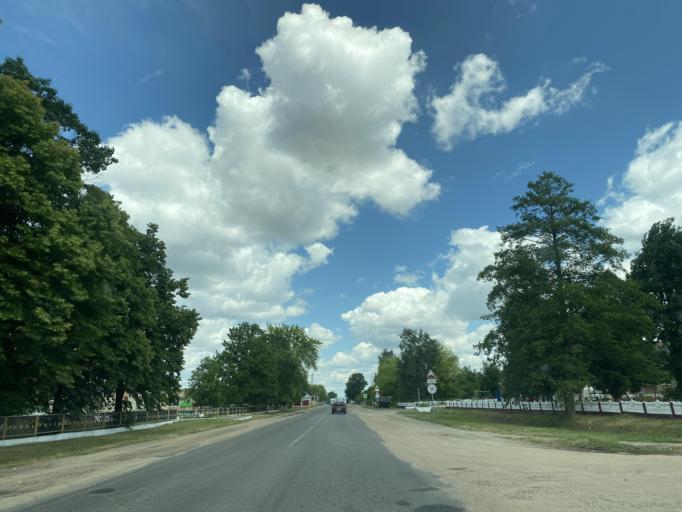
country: BY
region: Brest
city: Ivanava
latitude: 52.1656
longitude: 25.5487
